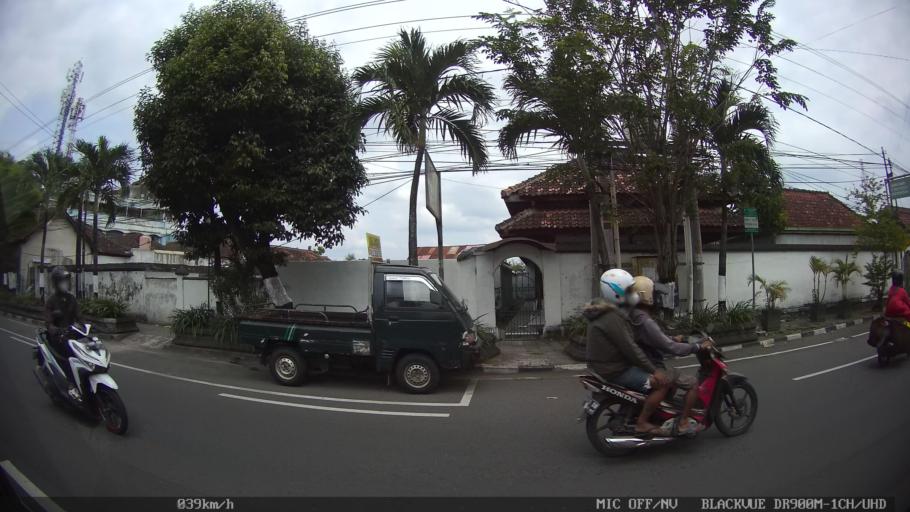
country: ID
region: Daerah Istimewa Yogyakarta
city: Yogyakarta
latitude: -7.8021
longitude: 110.3873
